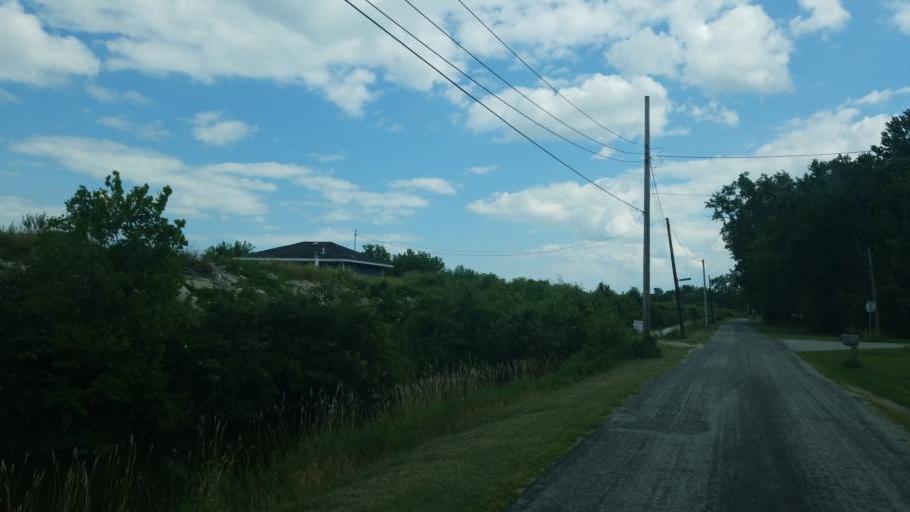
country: US
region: Ohio
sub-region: Lucas County
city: Curtice
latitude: 41.6667
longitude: -83.2689
